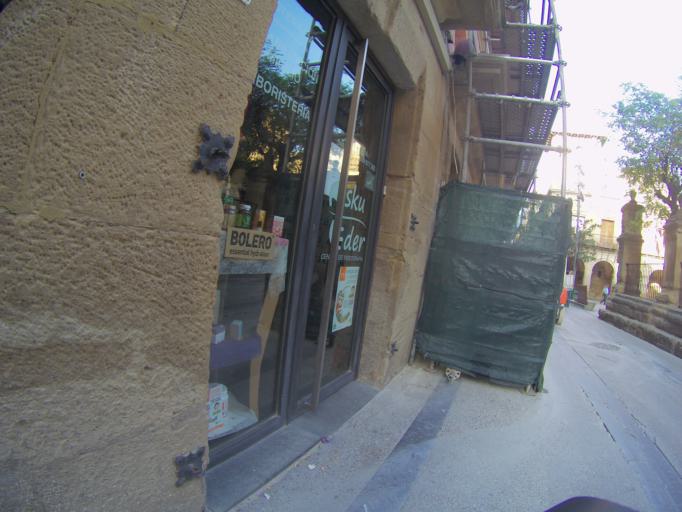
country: ES
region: Navarre
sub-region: Provincia de Navarra
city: Viana
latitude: 42.5151
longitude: -2.3717
